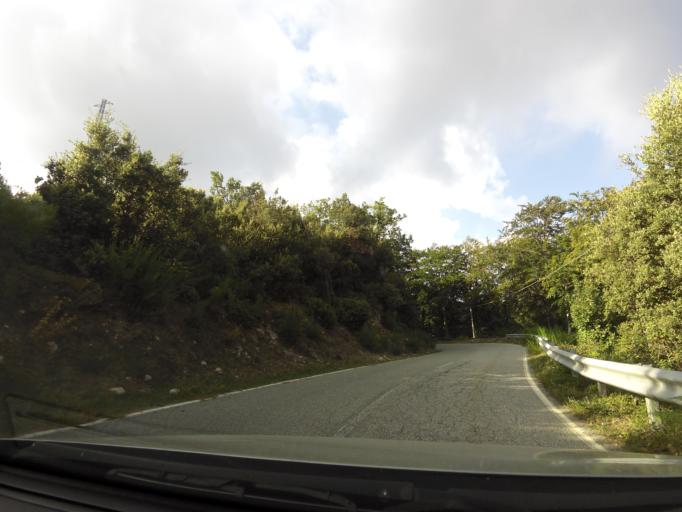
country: IT
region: Calabria
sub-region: Provincia di Vibo-Valentia
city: Nardodipace
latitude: 38.4798
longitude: 16.3821
